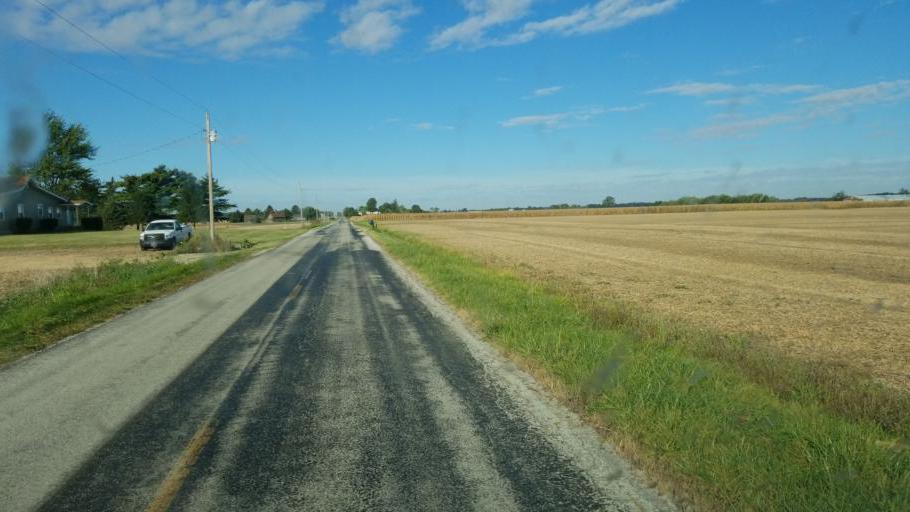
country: US
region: Ohio
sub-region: Marion County
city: Marion
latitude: 40.6885
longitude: -83.0502
